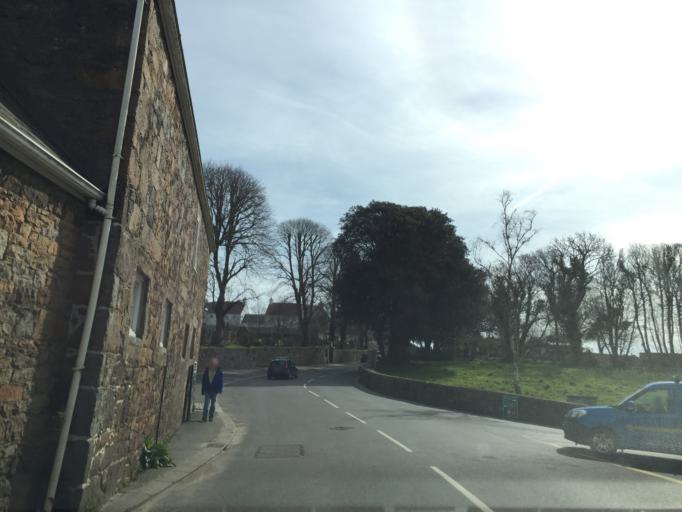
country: JE
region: St Helier
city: Saint Helier
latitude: 49.2336
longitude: -2.0929
